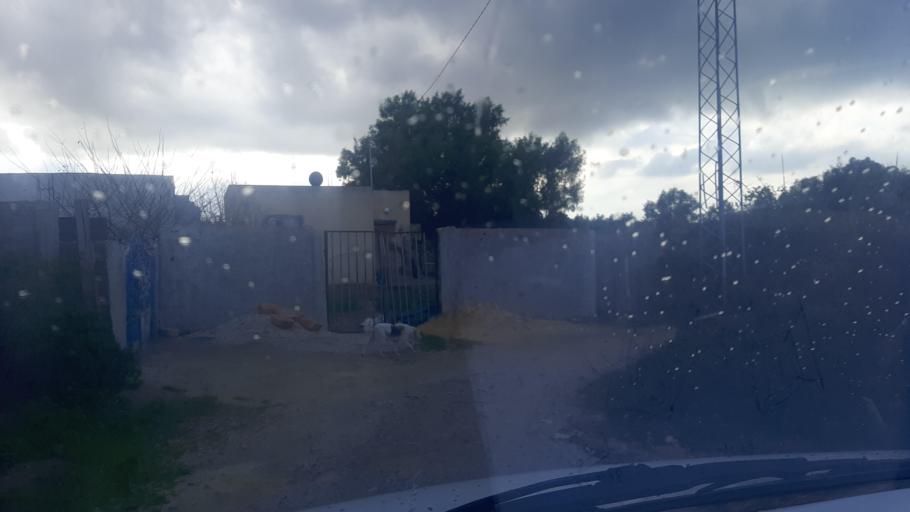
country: TN
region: Nabul
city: Qurbus
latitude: 36.7457
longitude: 10.5249
